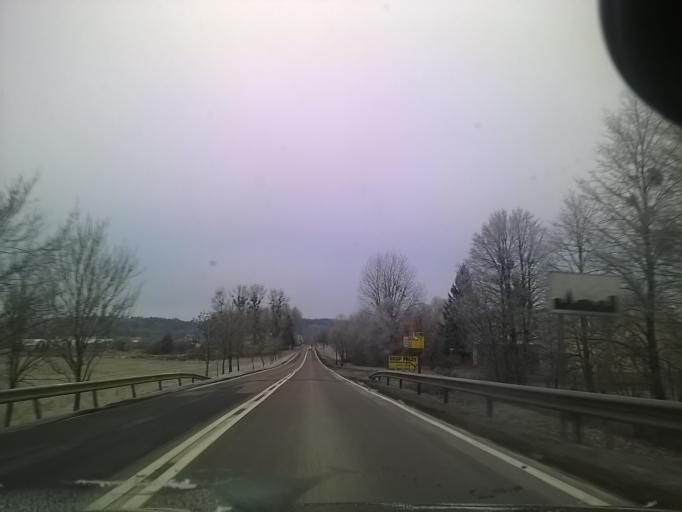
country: PL
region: Warmian-Masurian Voivodeship
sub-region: Powiat mragowski
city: Mragowo
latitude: 53.8435
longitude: 21.1542
